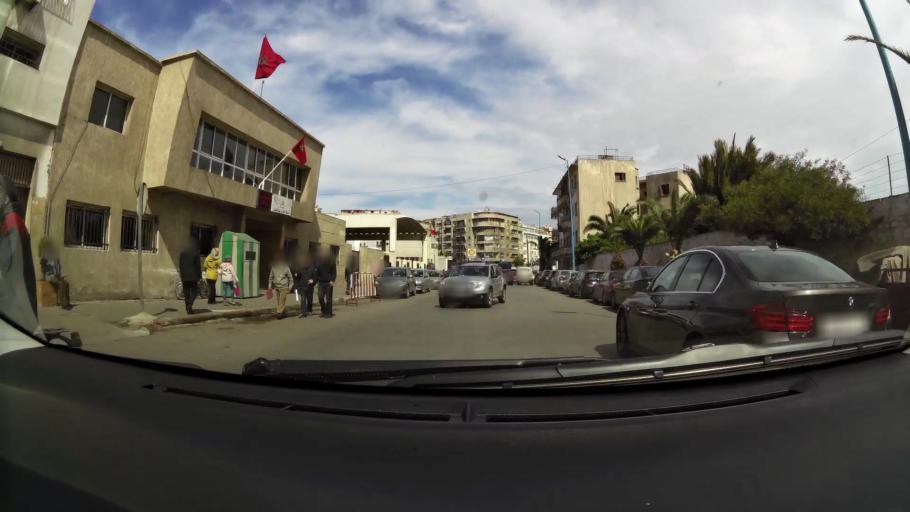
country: MA
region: Grand Casablanca
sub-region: Casablanca
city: Casablanca
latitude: 33.5852
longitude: -7.5836
